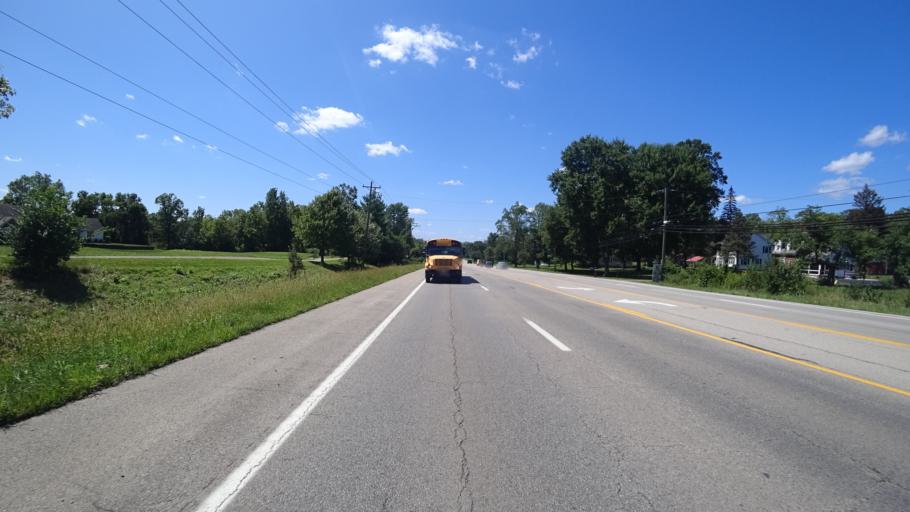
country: US
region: Ohio
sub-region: Butler County
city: New Miami
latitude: 39.4055
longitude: -84.5215
